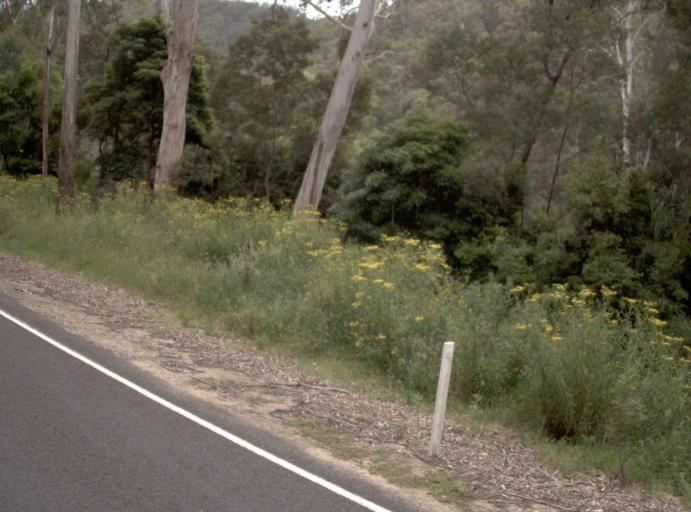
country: AU
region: New South Wales
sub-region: Bombala
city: Bombala
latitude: -37.4170
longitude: 149.1984
